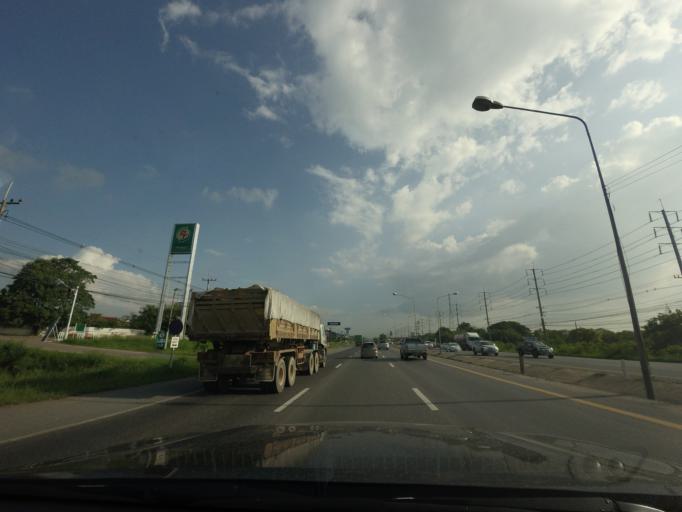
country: TH
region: Sara Buri
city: Chaloem Phra Kiat
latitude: 14.5816
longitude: 100.9004
